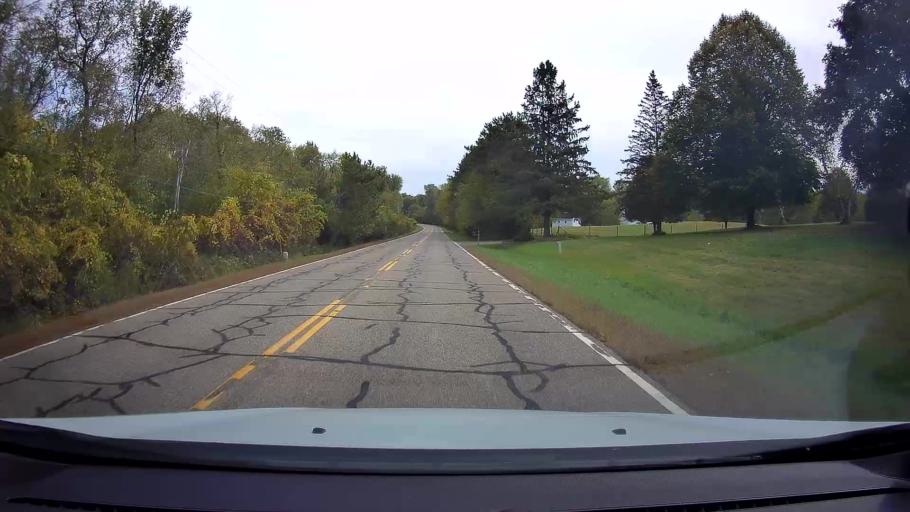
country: US
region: Minnesota
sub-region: Washington County
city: Stillwater
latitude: 45.1047
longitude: -92.8009
